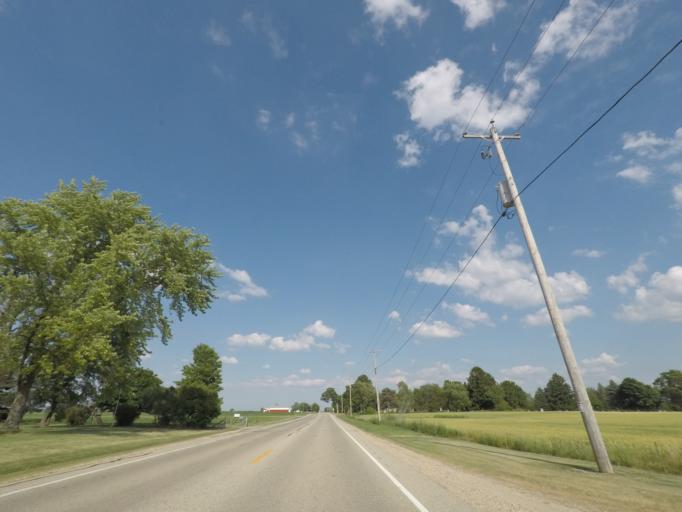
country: US
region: Wisconsin
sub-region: Walworth County
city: East Troy
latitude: 42.7929
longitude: -88.4712
